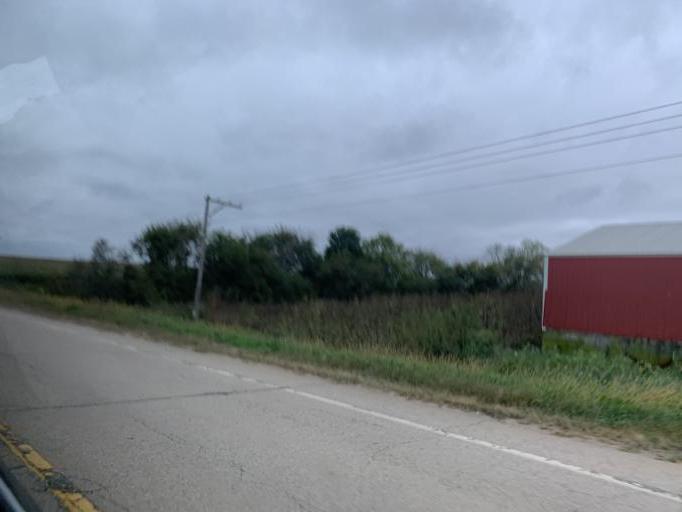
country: US
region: Wisconsin
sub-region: Grant County
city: Muscoda
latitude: 43.2198
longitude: -90.5135
